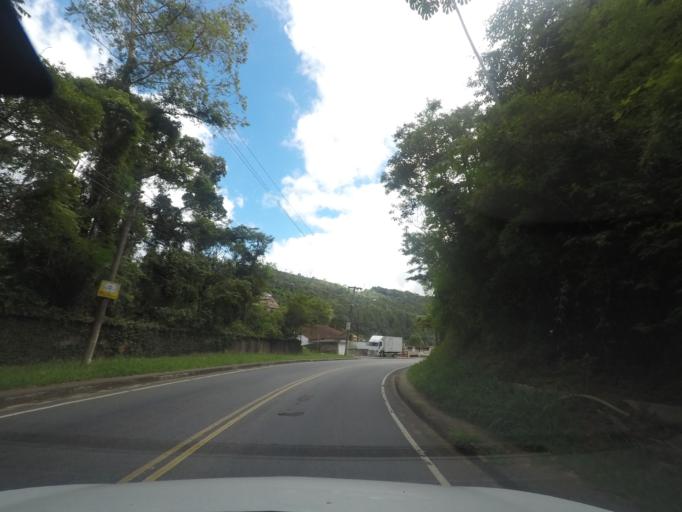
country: BR
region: Rio de Janeiro
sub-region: Teresopolis
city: Teresopolis
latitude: -22.3935
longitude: -42.9887
